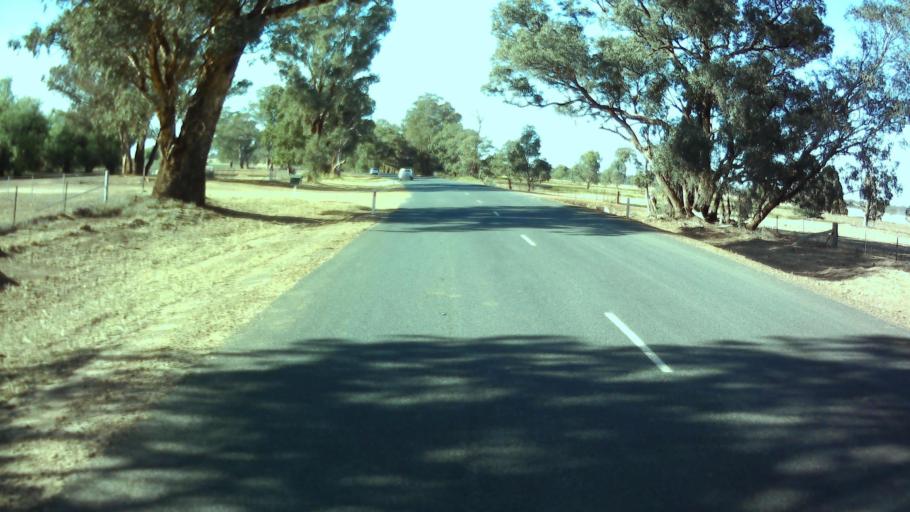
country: AU
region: New South Wales
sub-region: Weddin
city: Grenfell
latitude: -33.9795
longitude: 148.1406
